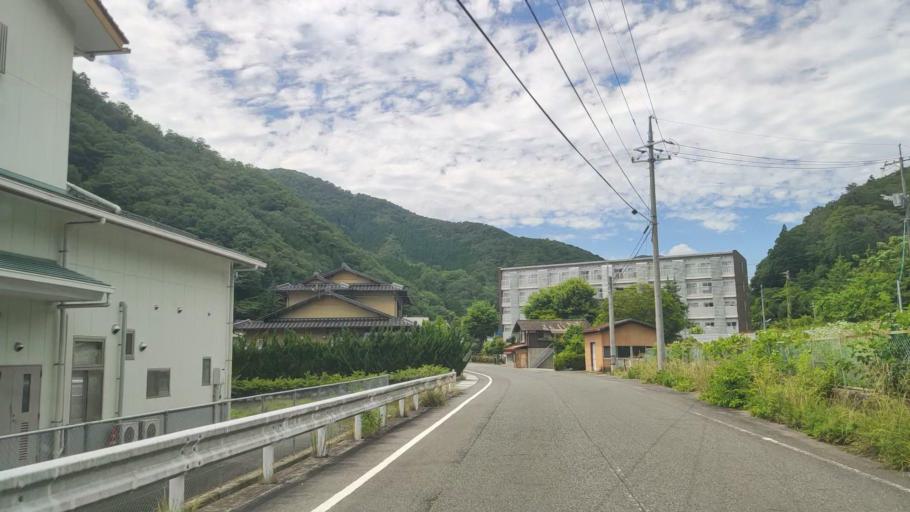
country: JP
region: Hyogo
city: Yamazakicho-nakabirose
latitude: 35.1088
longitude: 134.3277
